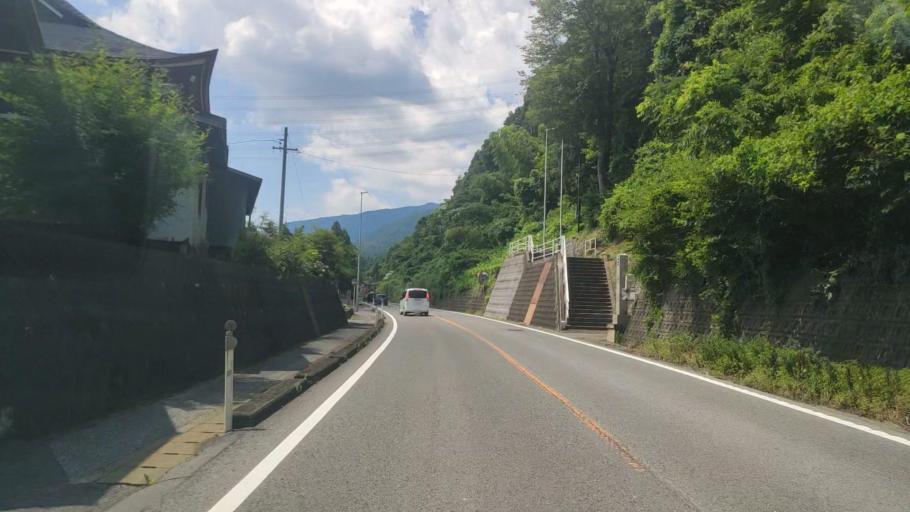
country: JP
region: Gifu
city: Tarui
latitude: 35.3775
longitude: 136.4413
